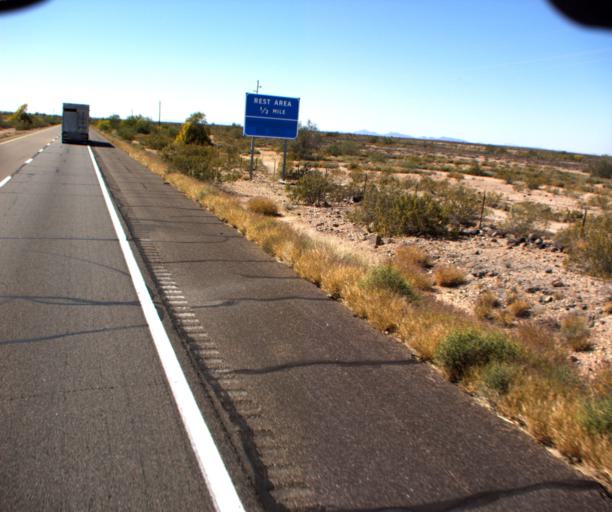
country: US
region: Arizona
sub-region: Maricopa County
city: Gila Bend
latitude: 32.8563
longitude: -113.2409
